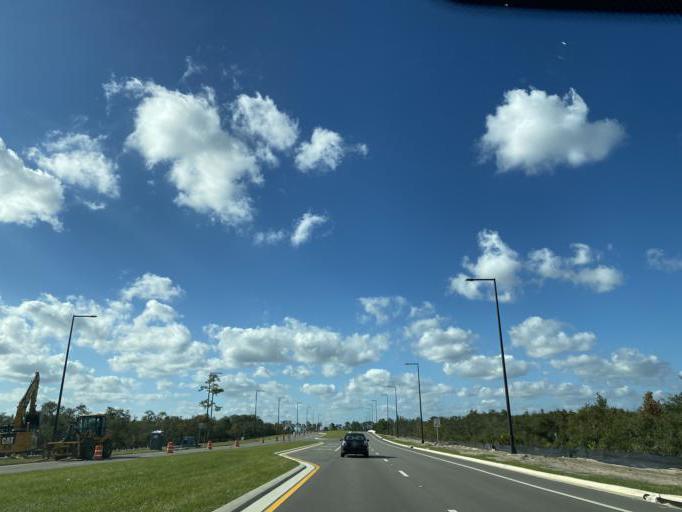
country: US
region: Florida
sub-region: Polk County
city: Citrus Ridge
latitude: 28.3808
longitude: -81.6282
